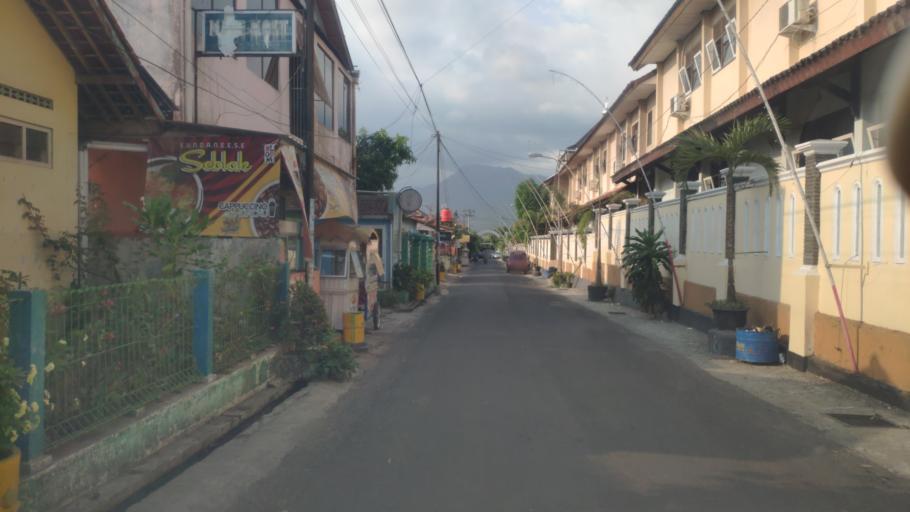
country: ID
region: Central Java
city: Wonosobo
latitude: -7.3950
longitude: 109.6945
